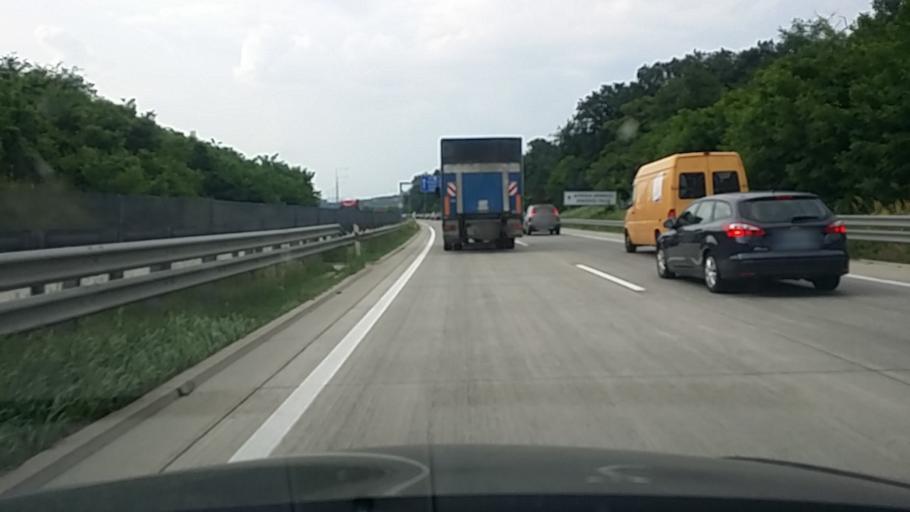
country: HU
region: Pest
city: Szada
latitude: 47.6036
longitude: 19.3208
